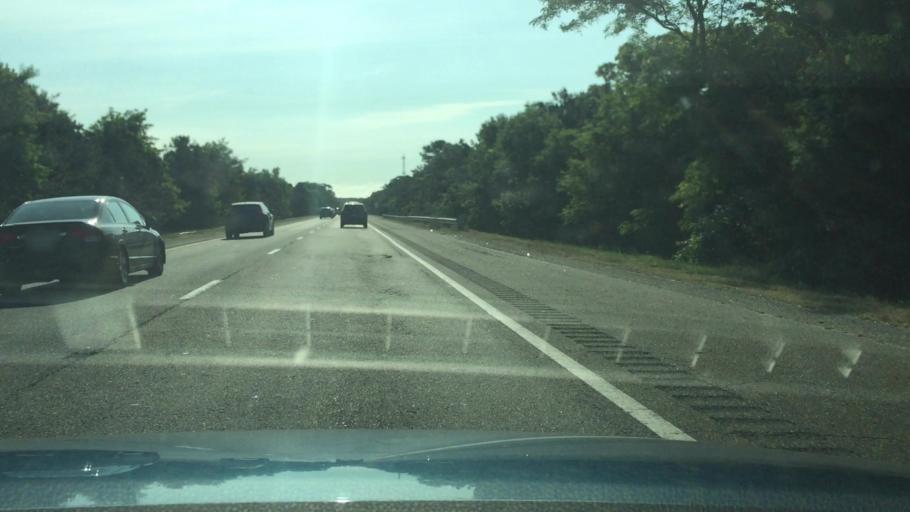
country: US
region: Massachusetts
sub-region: Barnstable County
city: Yarmouth
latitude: 41.6903
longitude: -70.2085
